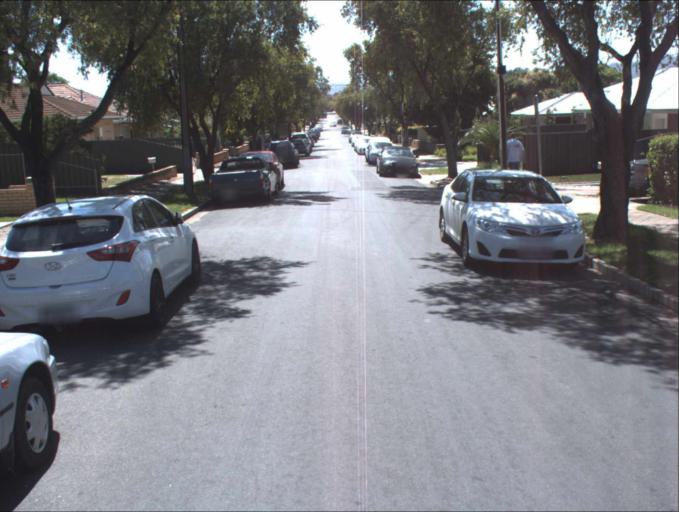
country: AU
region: South Australia
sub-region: Port Adelaide Enfield
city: Klemzig
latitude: -34.8769
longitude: 138.6344
